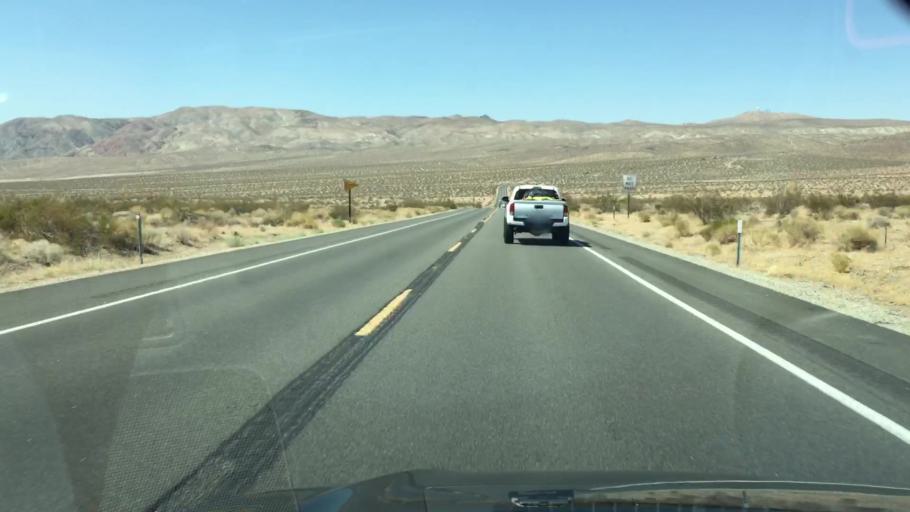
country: US
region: California
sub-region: Kern County
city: Ridgecrest
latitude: 35.4114
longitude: -117.6652
